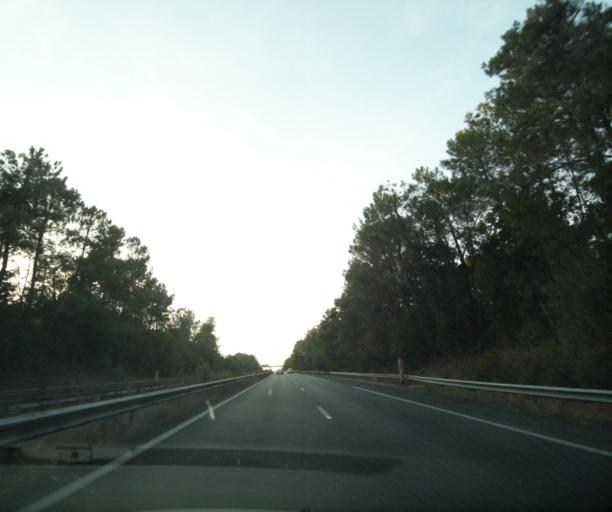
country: FR
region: Aquitaine
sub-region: Departement du Lot-et-Garonne
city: Fourques-sur-Garonne
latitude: 44.4401
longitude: 0.1159
